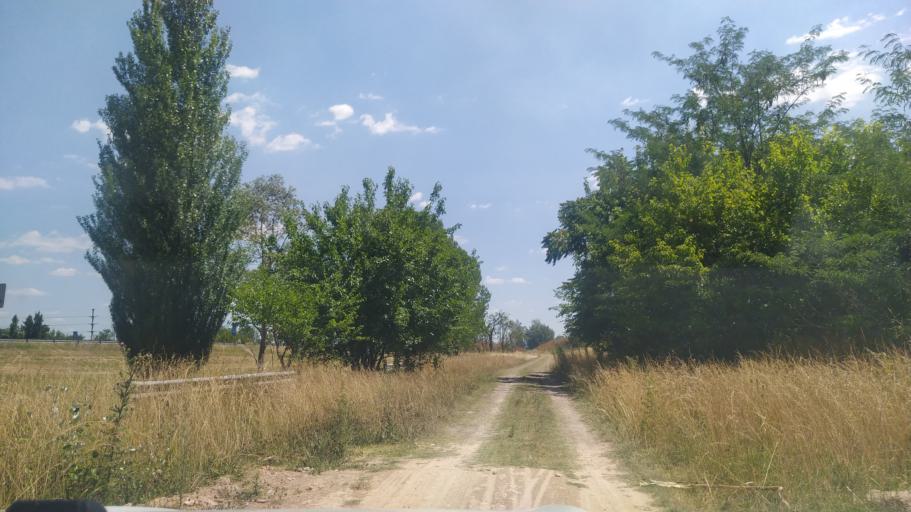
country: AR
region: Buenos Aires
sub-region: Partido de Ezeiza
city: Ezeiza
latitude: -34.9133
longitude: -58.6313
